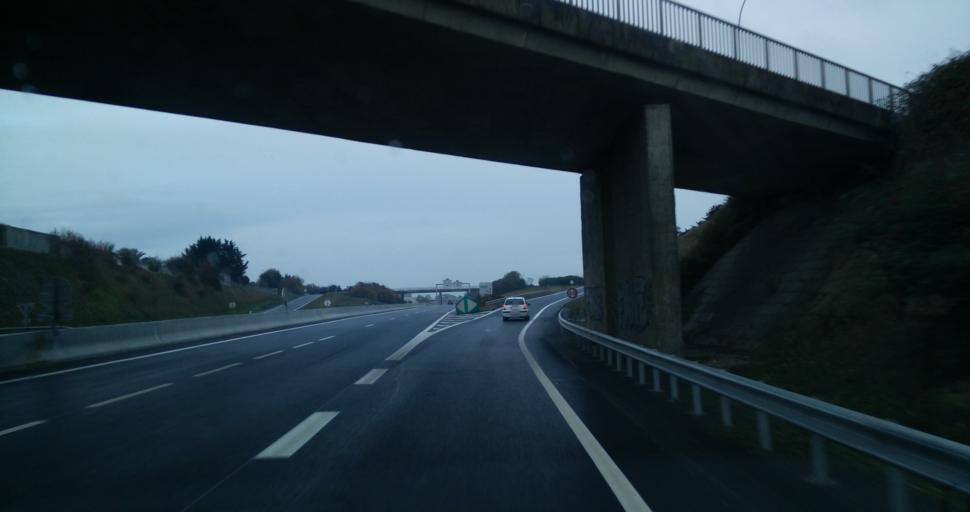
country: FR
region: Poitou-Charentes
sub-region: Departement de la Charente-Maritime
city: Lagord
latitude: 46.1720
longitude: -1.1956
